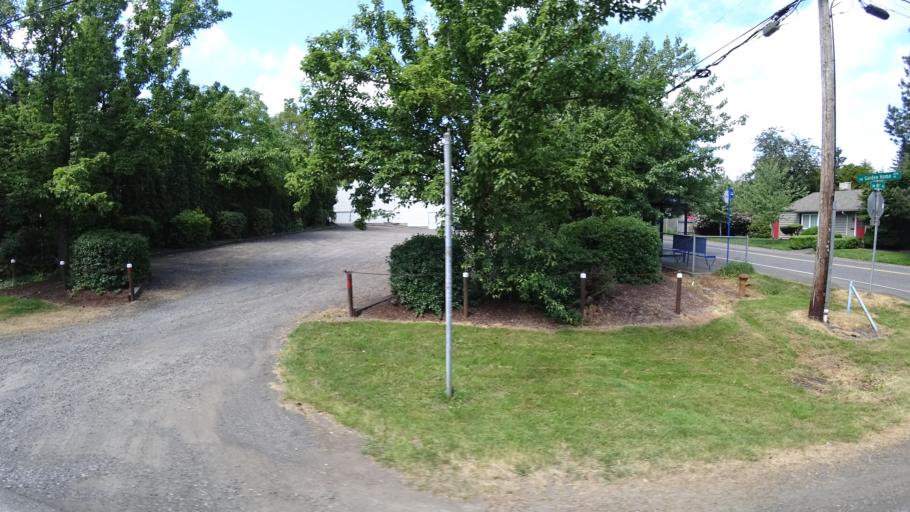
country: US
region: Oregon
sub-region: Washington County
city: Garden Home-Whitford
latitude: 45.4653
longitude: -122.7232
